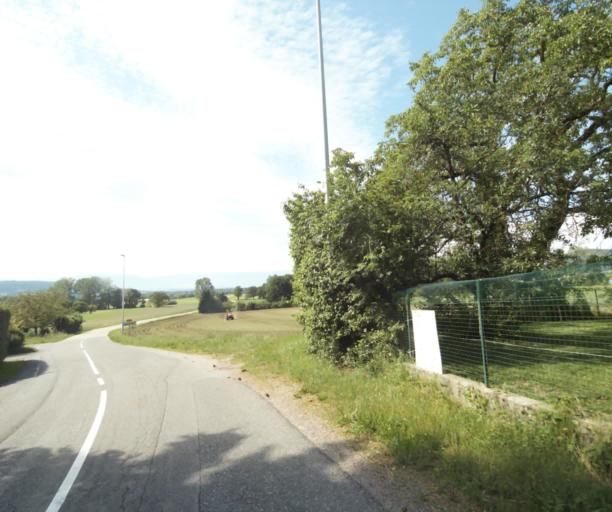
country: FR
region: Rhone-Alpes
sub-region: Departement de la Haute-Savoie
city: Perrignier
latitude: 46.2873
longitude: 6.4408
